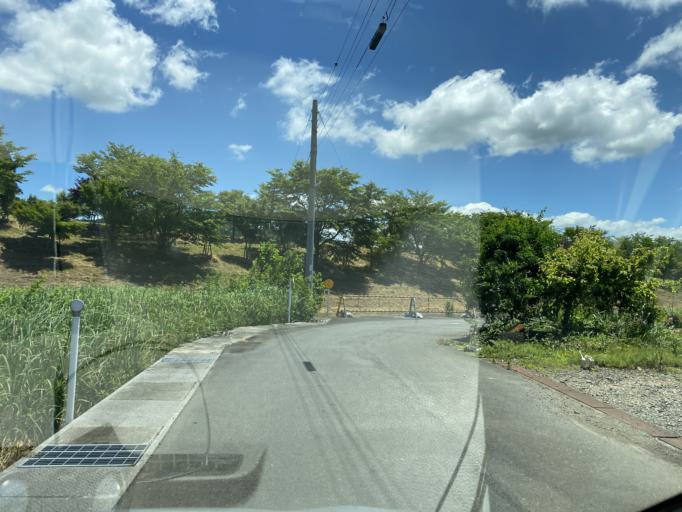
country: JP
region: Hyogo
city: Toyooka
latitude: 35.4915
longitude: 134.8081
